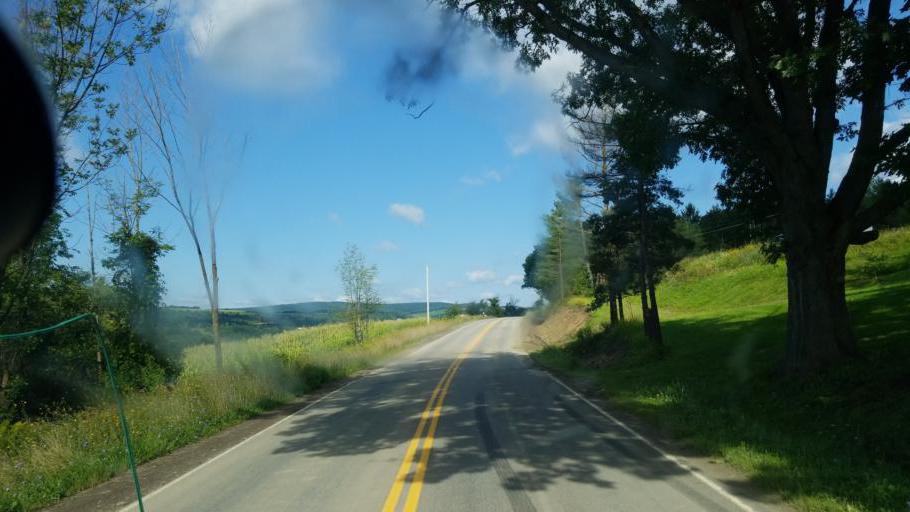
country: US
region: New York
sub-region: Steuben County
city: Hornell
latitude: 42.3025
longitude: -77.6345
